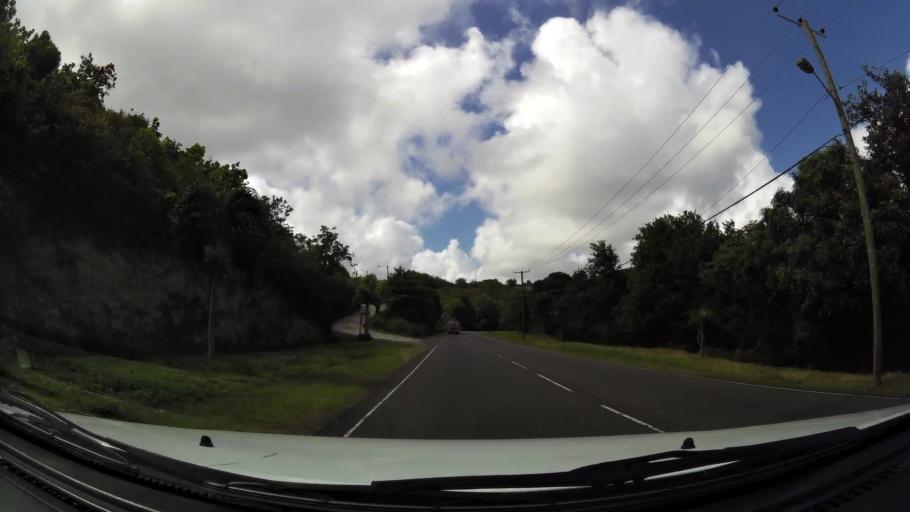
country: LC
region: Dennery Quarter
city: Dennery
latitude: 13.9201
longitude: -60.8962
